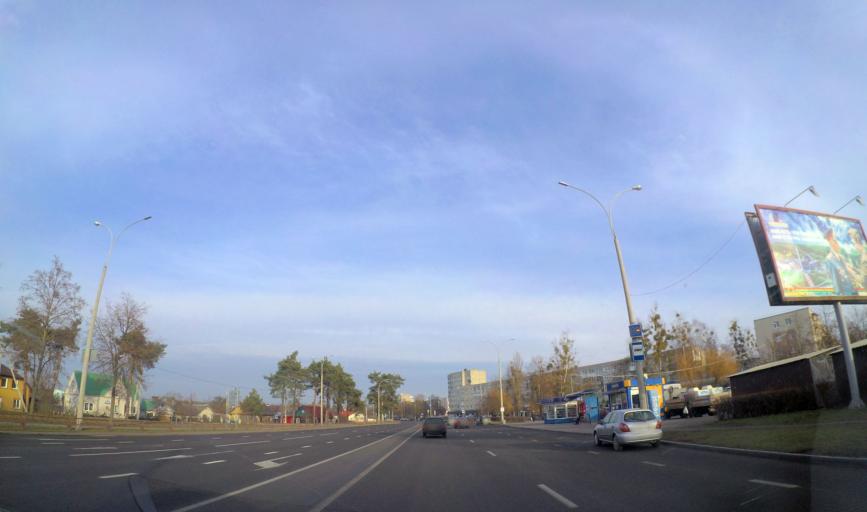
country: BY
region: Grodnenskaya
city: Hrodna
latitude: 53.6661
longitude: 23.7868
